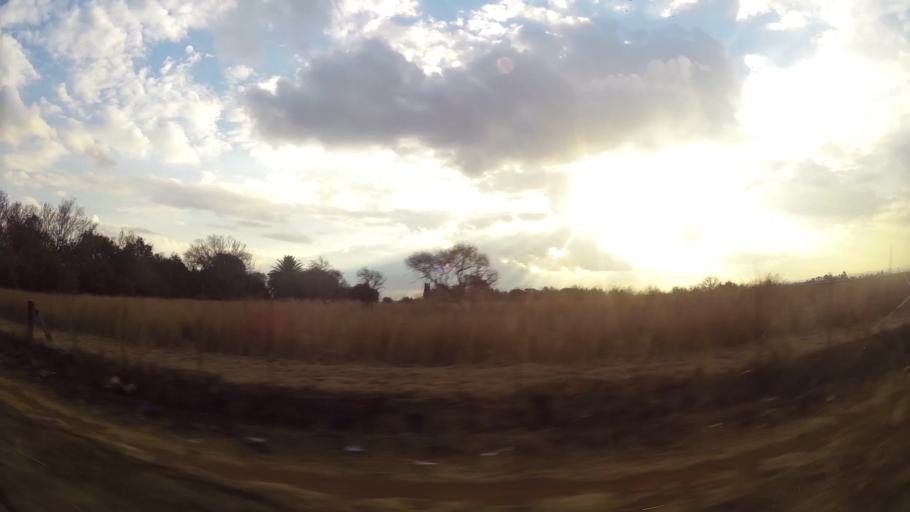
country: ZA
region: Gauteng
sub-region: Sedibeng District Municipality
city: Vanderbijlpark
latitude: -26.6358
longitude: 27.8073
